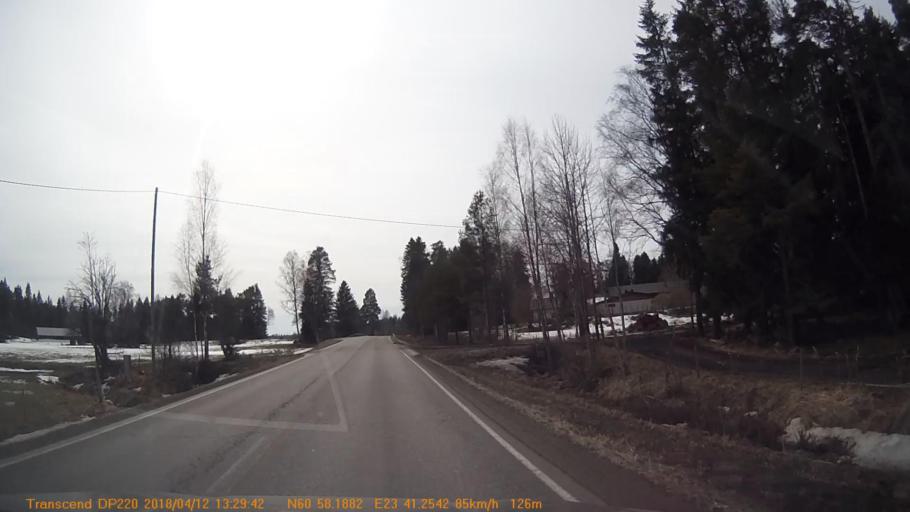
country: FI
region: Haeme
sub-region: Forssa
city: Forssa
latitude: 60.9695
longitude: 23.6872
